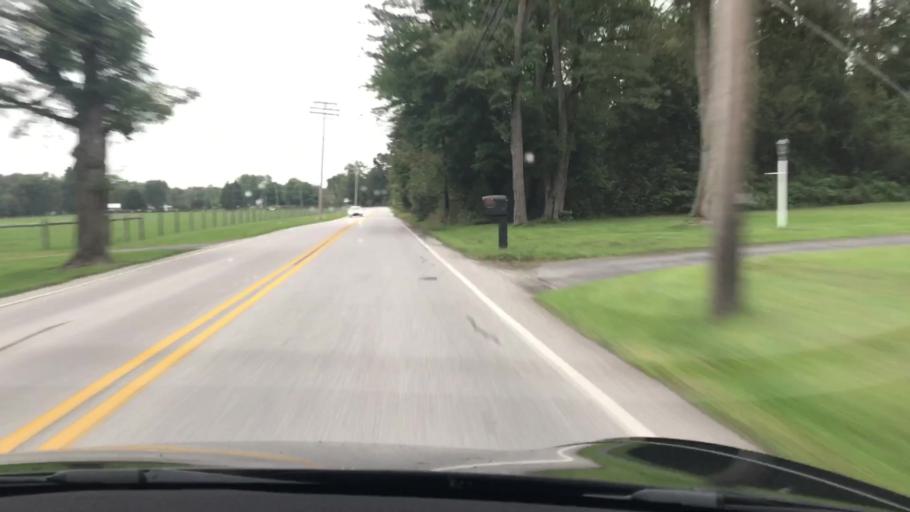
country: US
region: Pennsylvania
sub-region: York County
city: Dover
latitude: 39.9833
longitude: -76.8691
